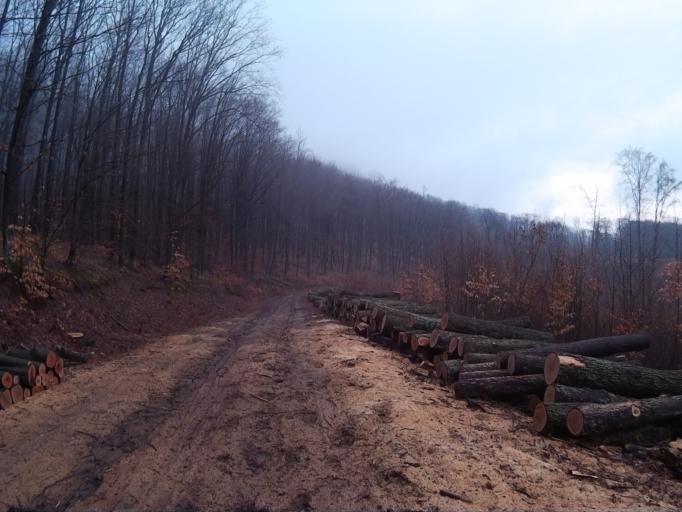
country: HU
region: Borsod-Abauj-Zemplen
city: Satoraljaujhely
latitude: 48.4228
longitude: 21.5705
